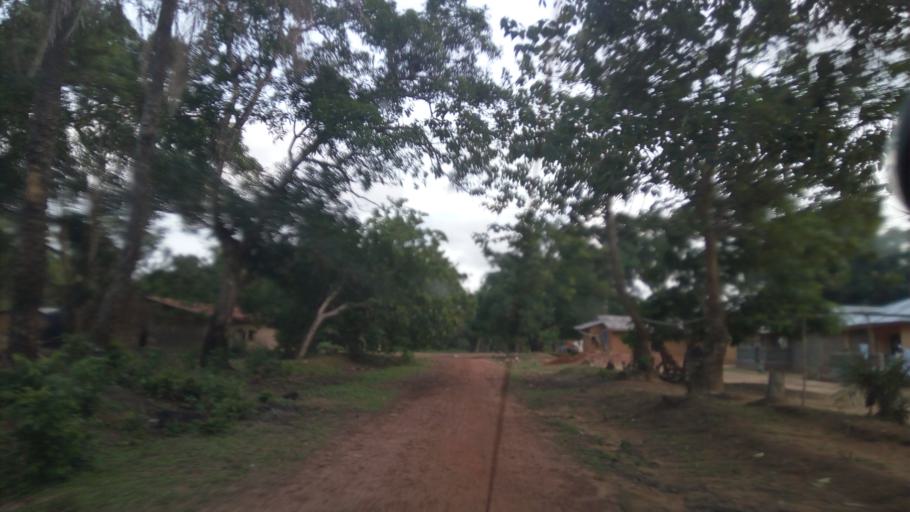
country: SL
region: Northern Province
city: Mambolo
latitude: 8.9940
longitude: -13.0132
